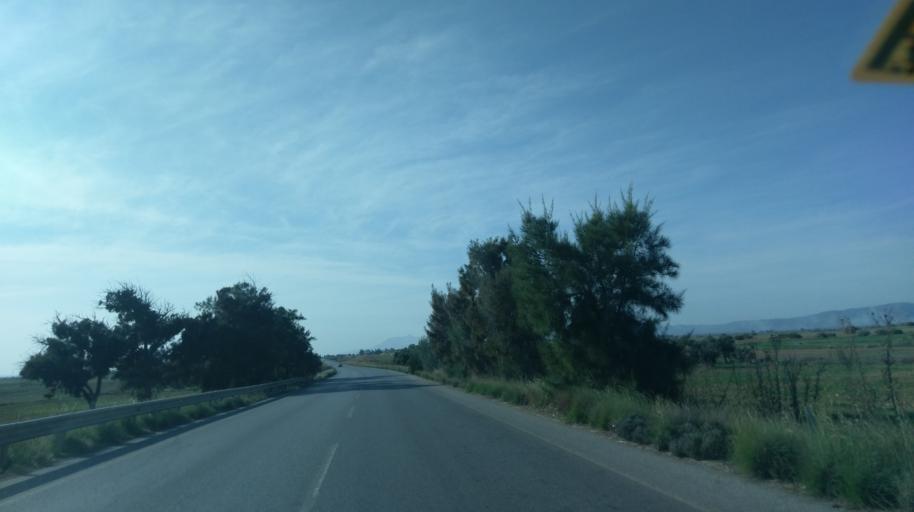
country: CY
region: Ammochostos
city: Lefkonoiko
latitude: 35.2613
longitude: 33.7764
